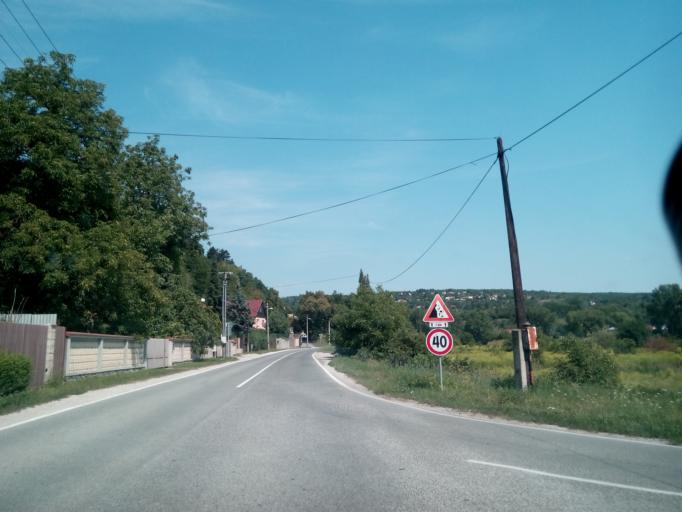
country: SK
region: Kosicky
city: Kosice
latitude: 48.7552
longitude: 21.2476
